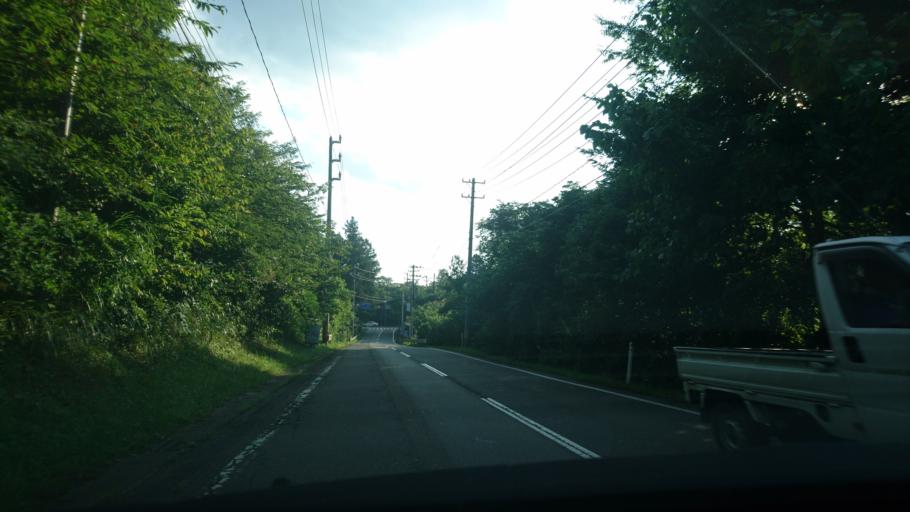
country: JP
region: Iwate
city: Ichinoseki
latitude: 38.9970
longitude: 141.2772
